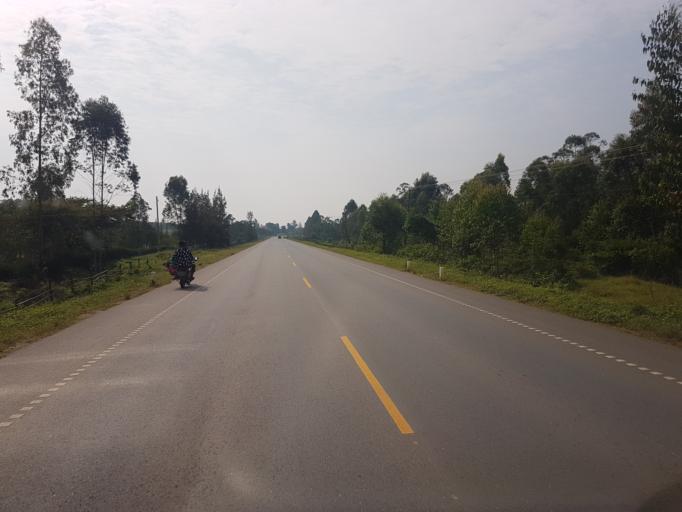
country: UG
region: Western Region
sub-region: Sheema District
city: Kibingo
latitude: -0.6349
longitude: 30.5313
